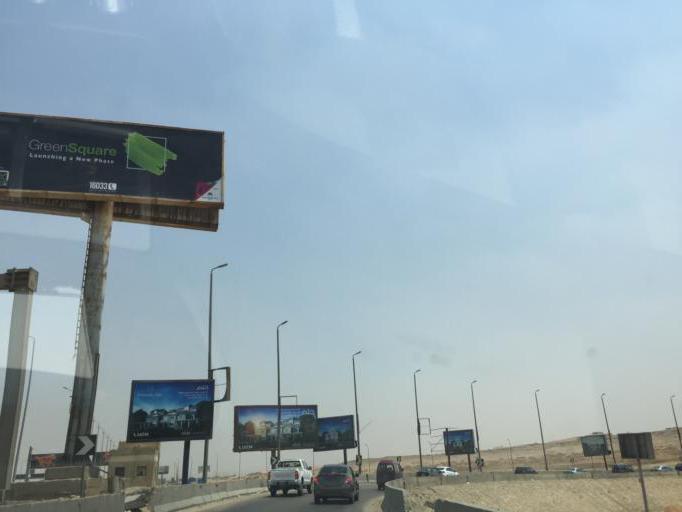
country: EG
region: Muhafazat al Qalyubiyah
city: Al Khankah
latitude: 30.0809
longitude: 31.4361
